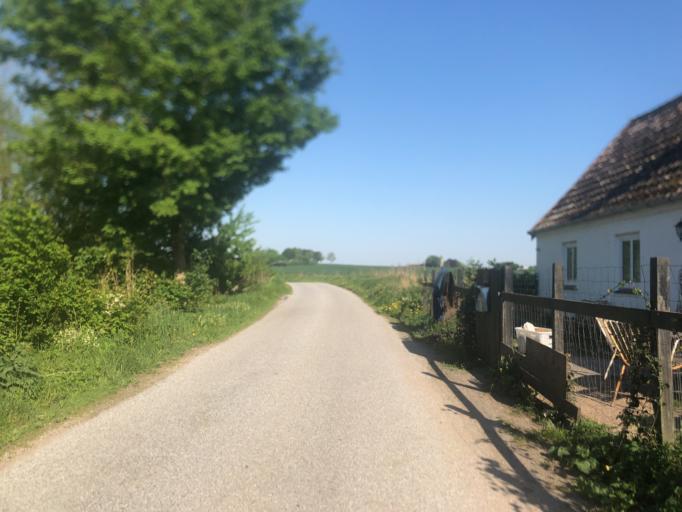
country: DK
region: Zealand
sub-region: Ringsted Kommune
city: Ringsted
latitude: 55.4809
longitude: 11.7845
